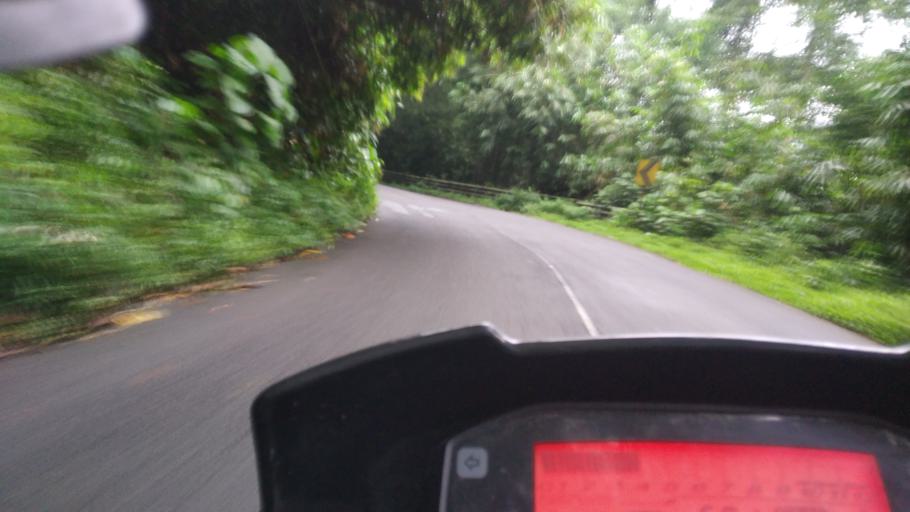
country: IN
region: Kerala
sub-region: Idukki
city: Kuttampuzha
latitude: 10.0636
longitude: 76.7929
